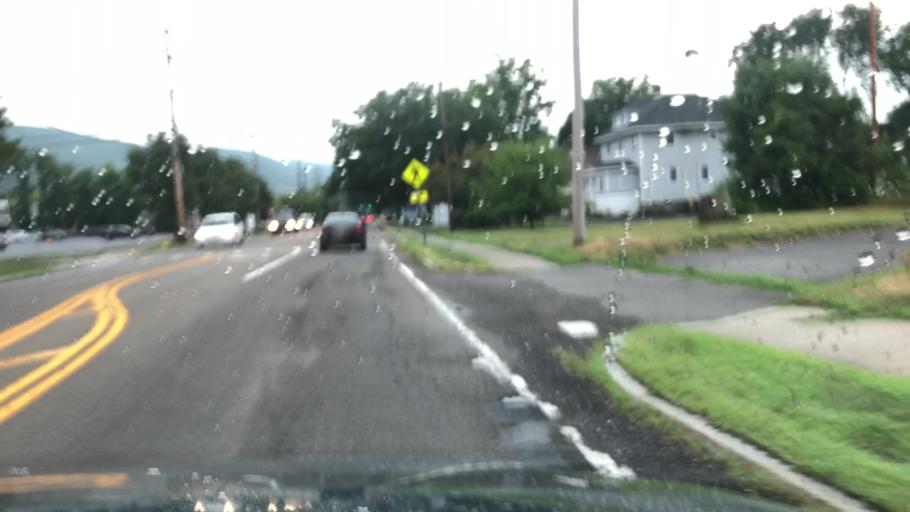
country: US
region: New York
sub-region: Dutchess County
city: Fishkill
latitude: 41.5332
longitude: -73.9056
